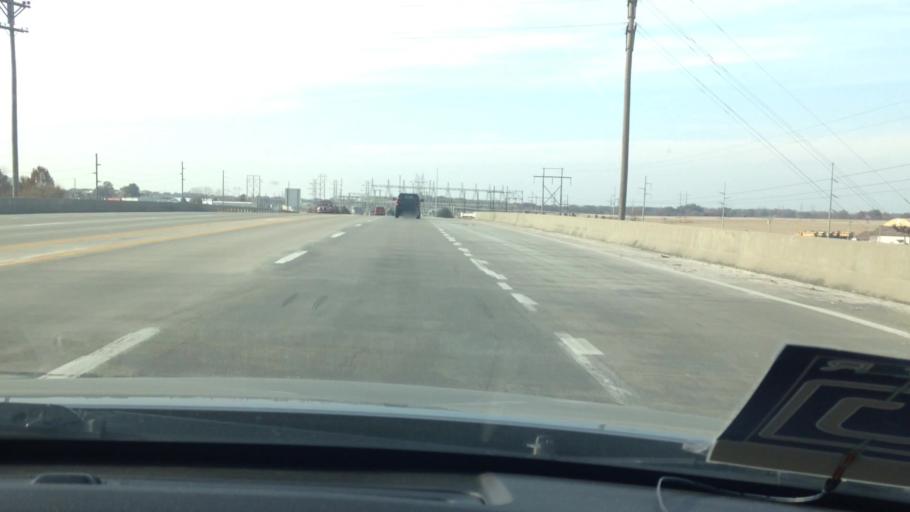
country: US
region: Missouri
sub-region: Henry County
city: Clinton
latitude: 38.3855
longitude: -93.7549
